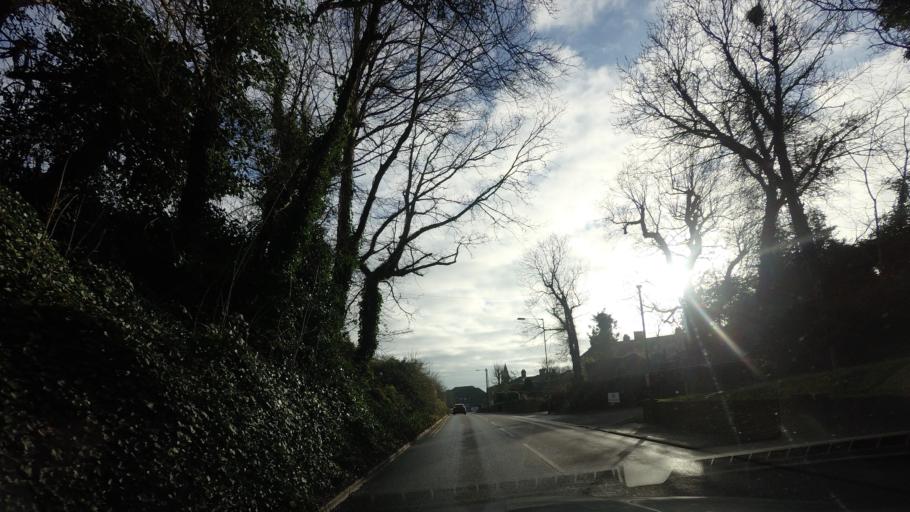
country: GB
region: England
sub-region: East Sussex
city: Battle
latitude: 50.9197
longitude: 0.4817
